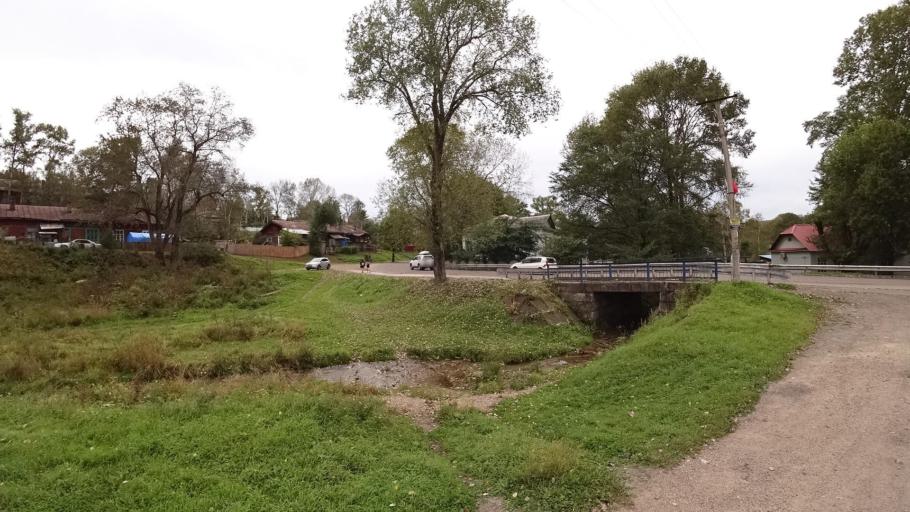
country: RU
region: Jewish Autonomous Oblast
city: Khingansk
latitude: 49.0194
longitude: 131.0633
